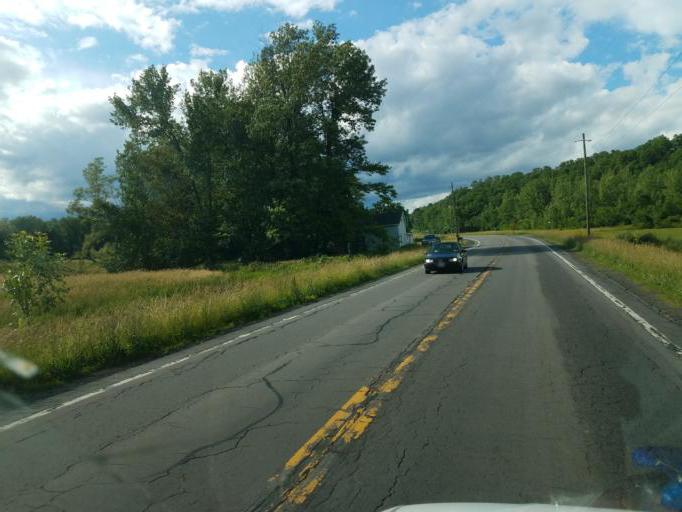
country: US
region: New York
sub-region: Wayne County
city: Clyde
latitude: 43.0403
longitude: -76.8627
